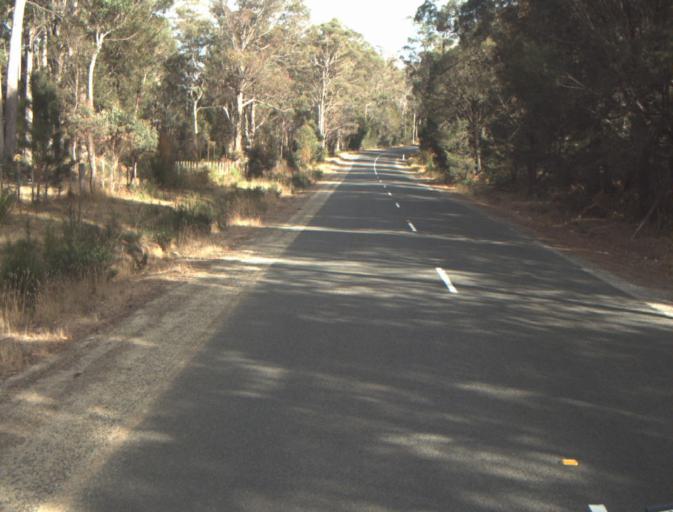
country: AU
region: Tasmania
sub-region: Dorset
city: Bridport
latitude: -41.1248
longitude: 147.2088
